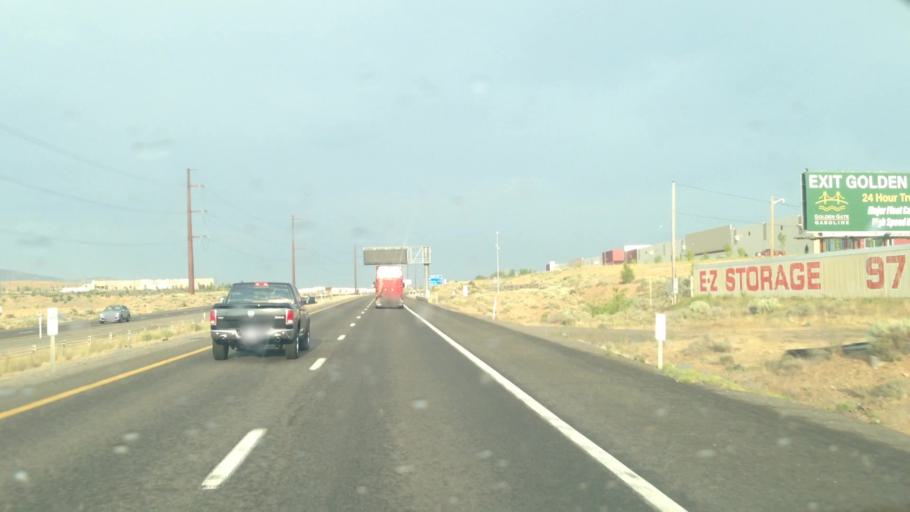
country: US
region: Nevada
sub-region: Washoe County
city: Lemmon Valley
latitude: 39.6156
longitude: -119.8651
